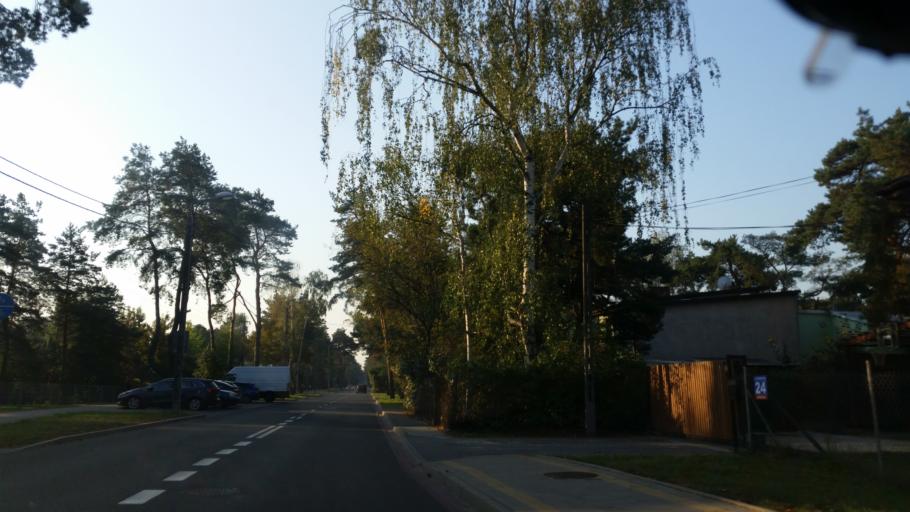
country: PL
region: Masovian Voivodeship
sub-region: Powiat otwocki
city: Jozefow
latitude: 52.1442
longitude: 21.2146
